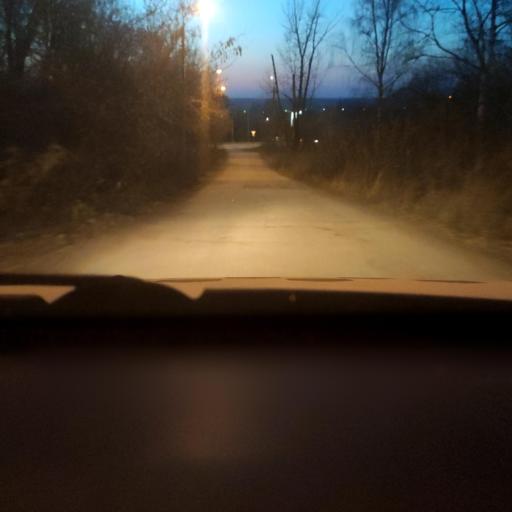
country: RU
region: Perm
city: Perm
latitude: 58.0573
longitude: 56.3389
